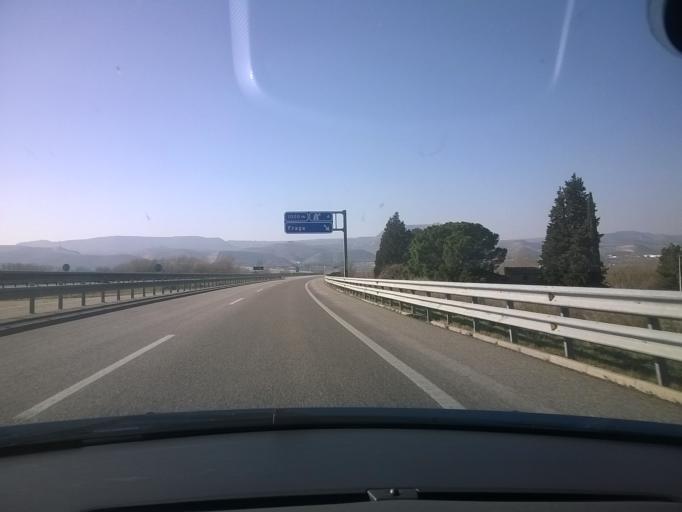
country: ES
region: Aragon
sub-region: Provincia de Huesca
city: Fraga
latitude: 41.4909
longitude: 0.3543
